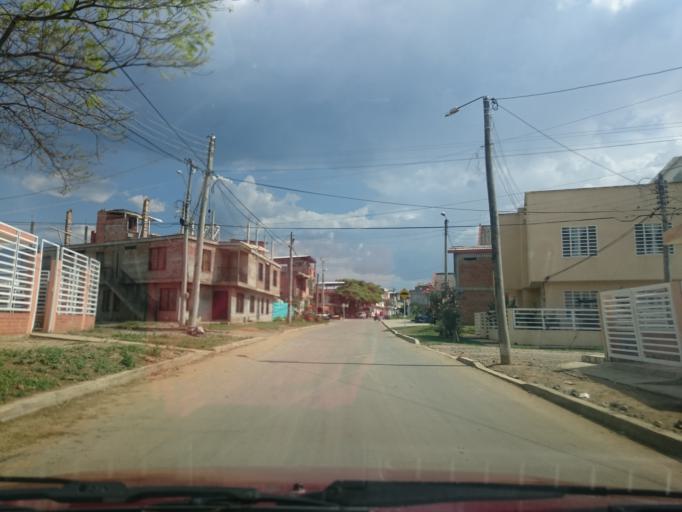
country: CO
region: Cauca
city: Santander de Quilichao
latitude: 3.0158
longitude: -76.4853
